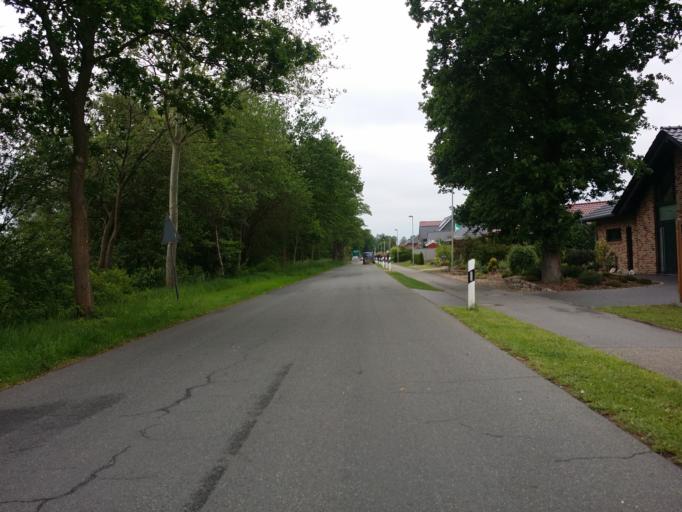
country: DE
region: Lower Saxony
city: Hatten
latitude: 53.1141
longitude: 8.3410
